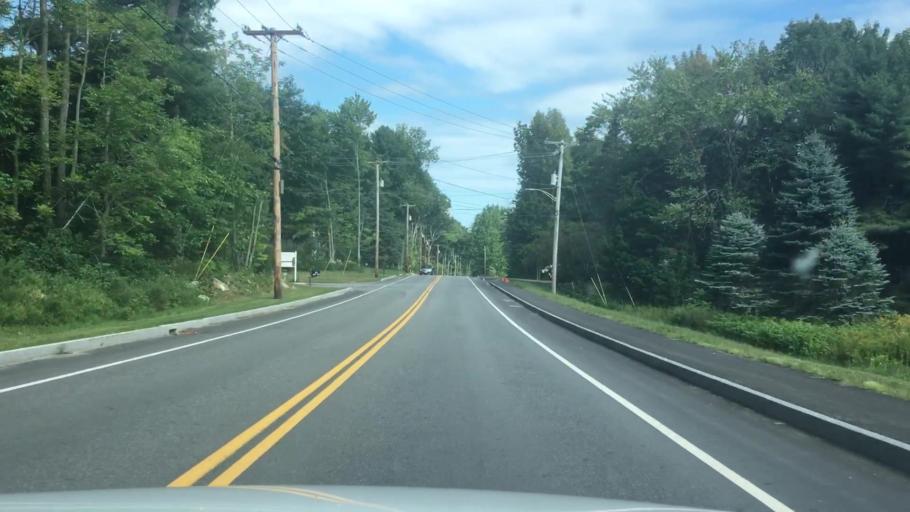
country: US
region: Maine
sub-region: Androscoggin County
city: Auburn
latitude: 44.1125
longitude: -70.2504
